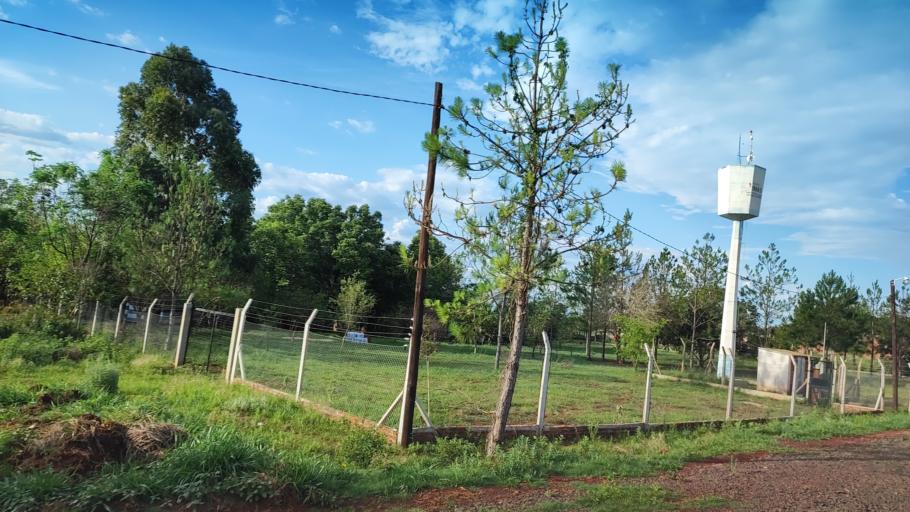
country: AR
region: Misiones
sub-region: Departamento de Capital
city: Posadas
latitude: -27.4471
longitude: -55.9633
